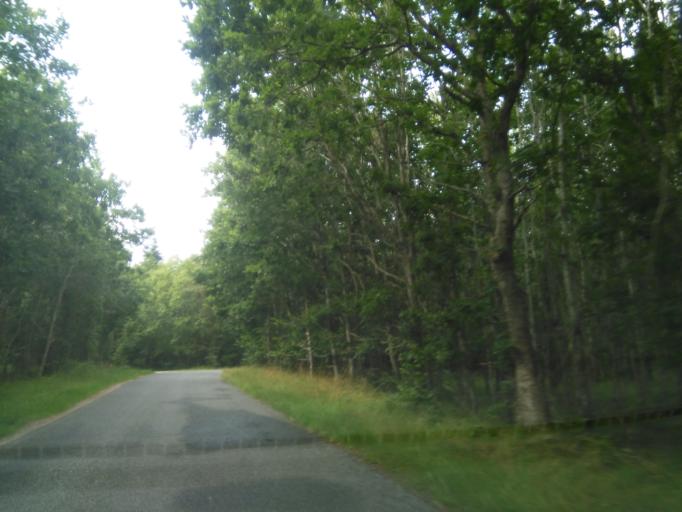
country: DK
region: Central Jutland
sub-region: Odder Kommune
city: Odder
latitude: 55.8848
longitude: 10.0493
